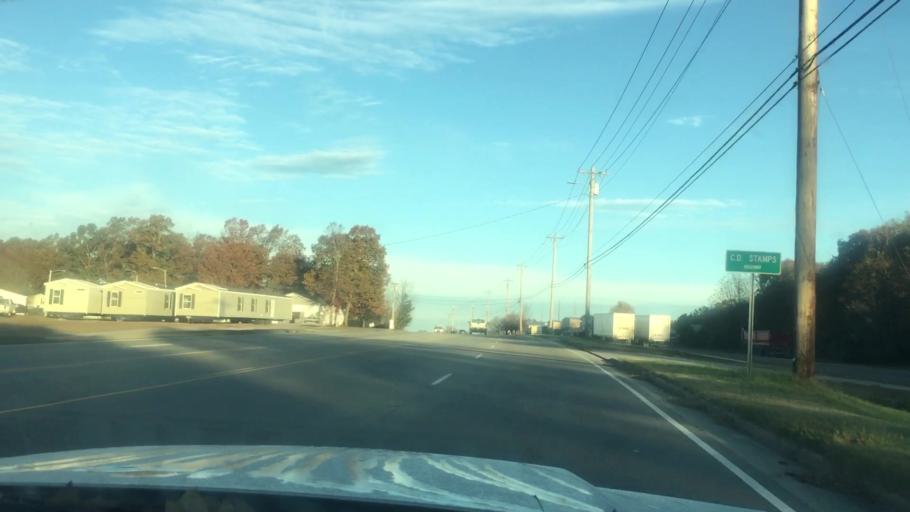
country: US
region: Tennessee
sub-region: Coffee County
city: Tullahoma
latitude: 35.3448
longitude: -86.1943
